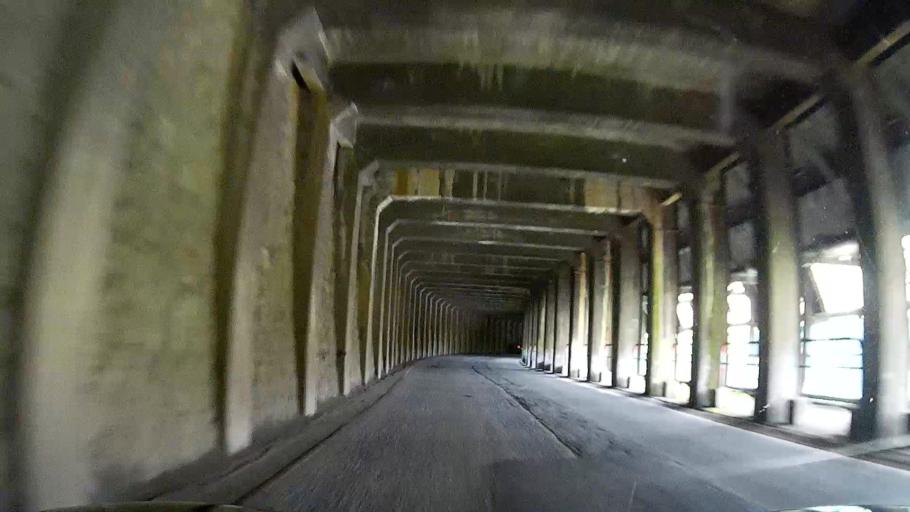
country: JP
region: Niigata
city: Tokamachi
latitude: 36.9977
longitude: 138.6167
